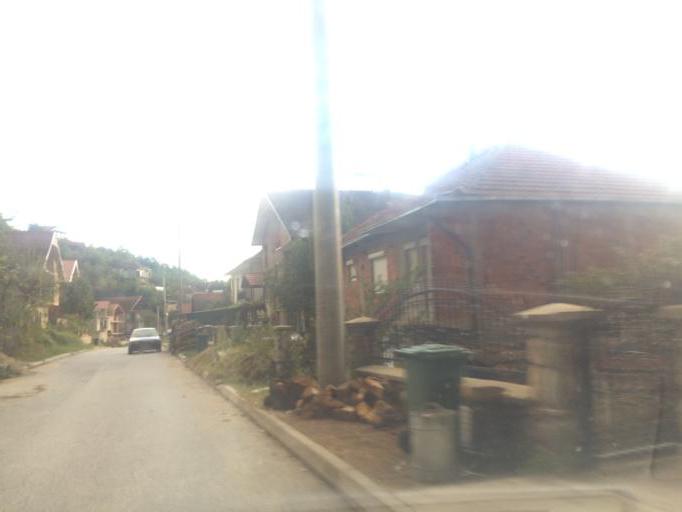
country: MK
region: Makedonska Kamenica
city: Makedonska Kamenica
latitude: 42.0164
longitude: 22.5924
